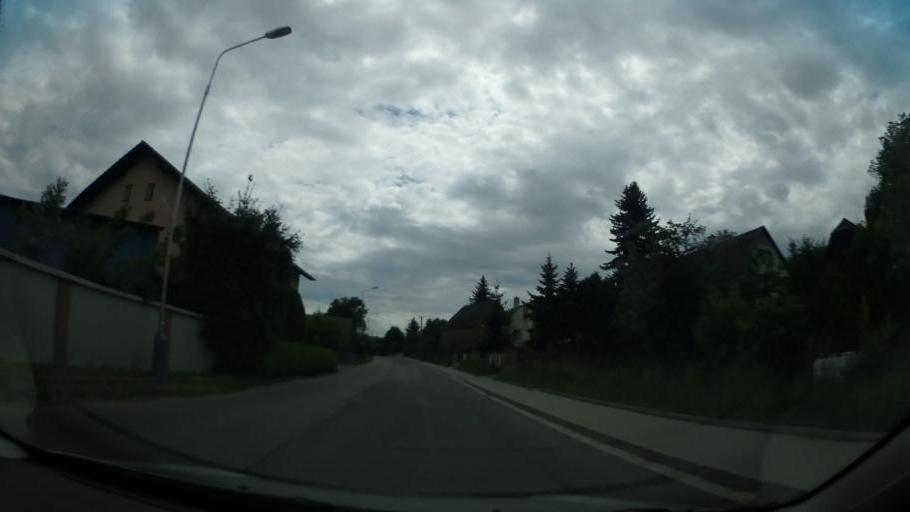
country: CZ
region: Pardubicky
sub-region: Okres Svitavy
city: Moravska Trebova
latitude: 49.7715
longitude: 16.6635
